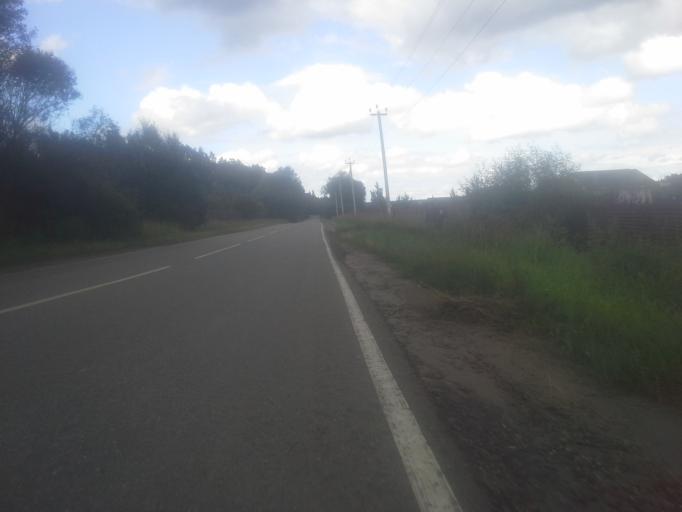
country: RU
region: Moskovskaya
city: Karinskoye
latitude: 55.6625
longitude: 36.6410
